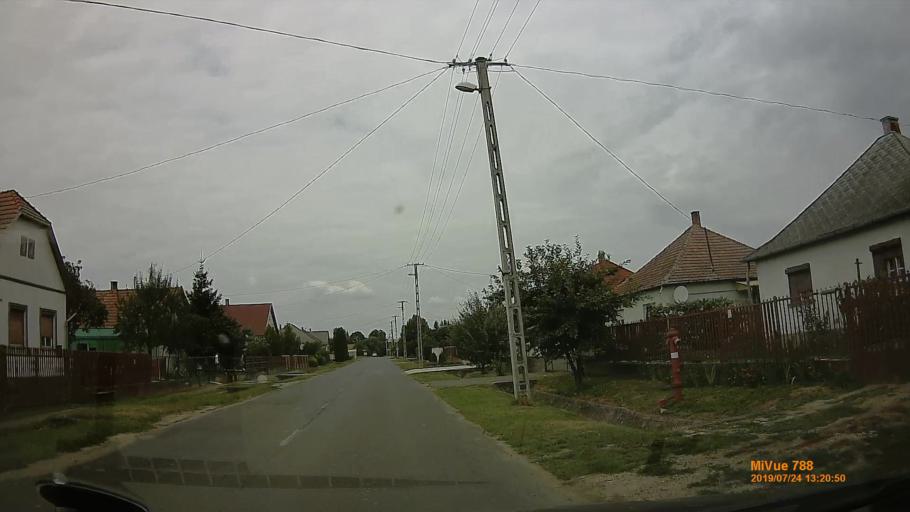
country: HU
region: Szabolcs-Szatmar-Bereg
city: Vasarosnameny
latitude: 48.2033
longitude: 22.4146
